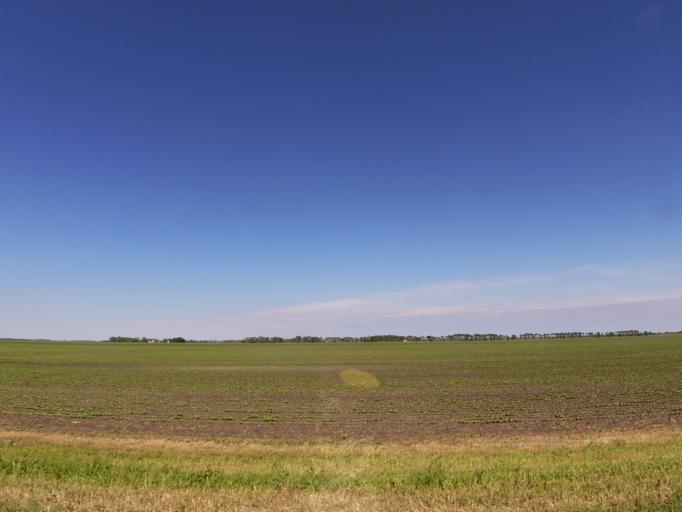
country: US
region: North Dakota
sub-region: Walsh County
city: Grafton
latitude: 48.3441
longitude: -97.2558
